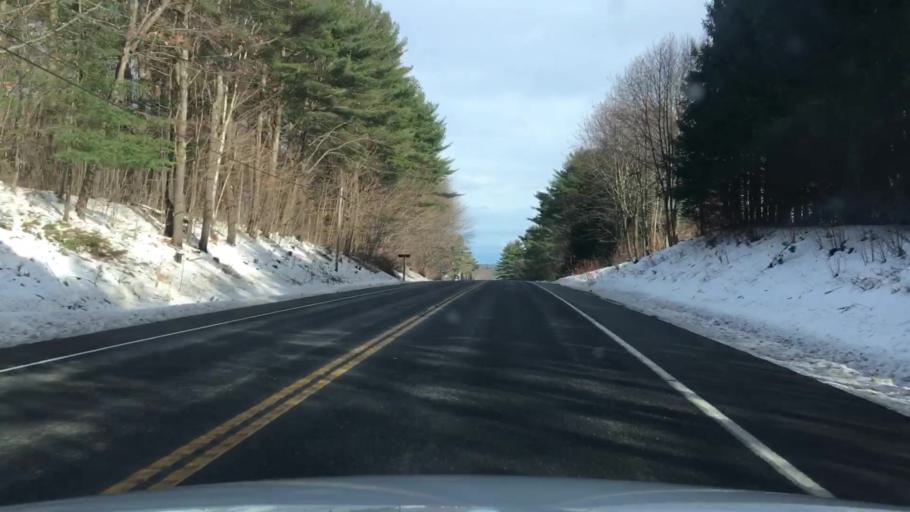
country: US
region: Maine
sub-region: Androscoggin County
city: Greene
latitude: 44.1886
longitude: -70.1501
